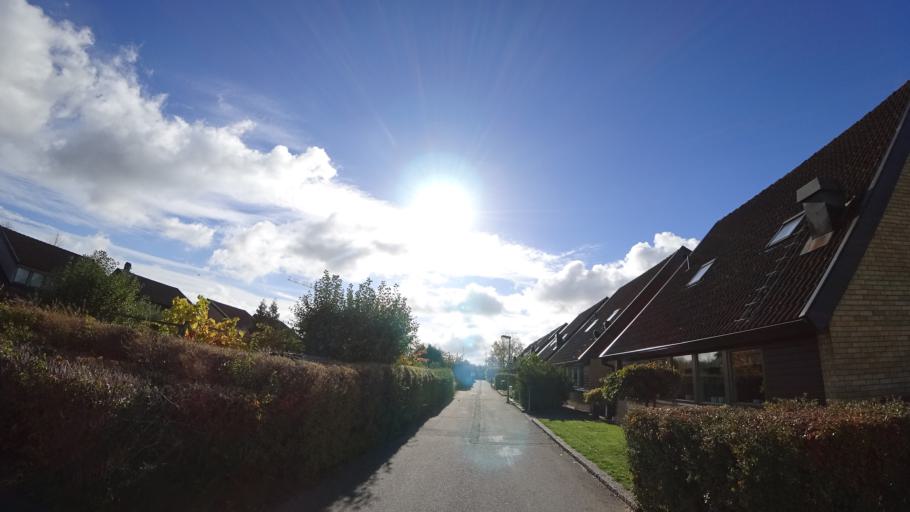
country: SE
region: Skane
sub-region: Staffanstorps Kommun
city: Staffanstorp
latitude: 55.6331
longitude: 13.1981
